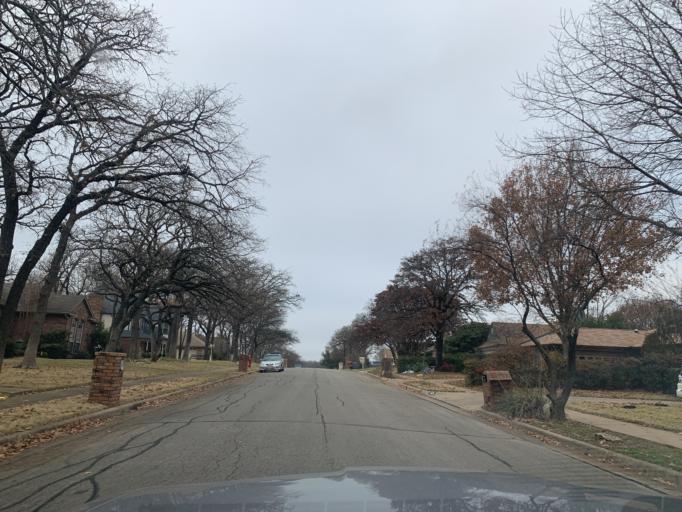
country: US
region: Texas
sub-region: Tarrant County
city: Bedford
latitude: 32.8344
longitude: -97.1472
